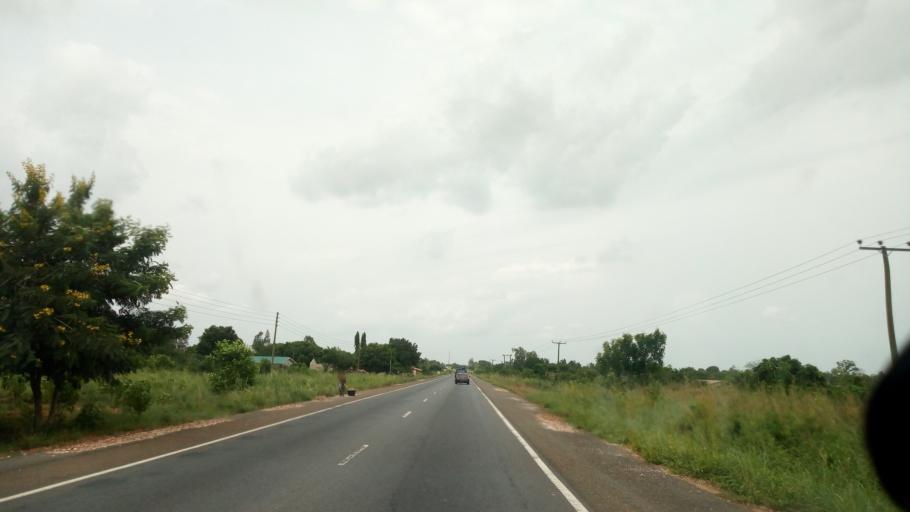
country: GH
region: Volta
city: Keta
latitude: 6.0653
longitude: 0.8961
